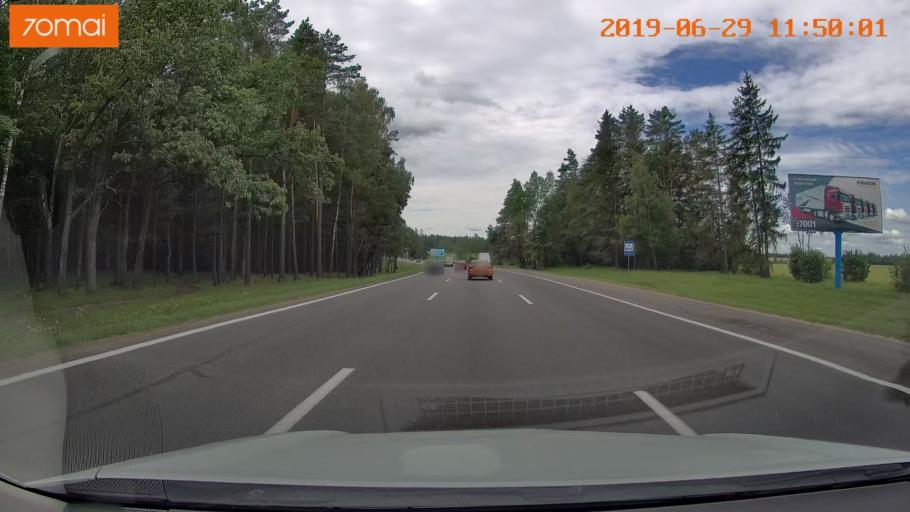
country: BY
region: Minsk
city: Azyartso
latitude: 53.7967
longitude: 27.3704
